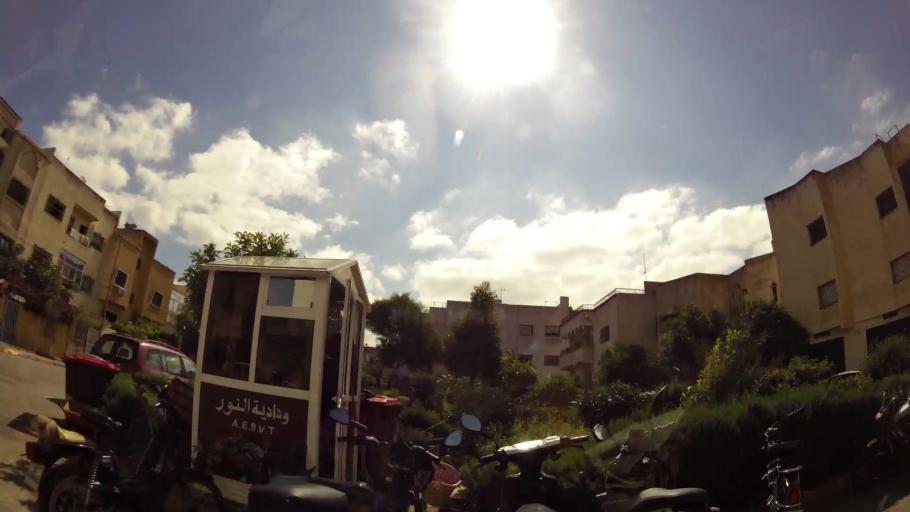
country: MA
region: Fes-Boulemane
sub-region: Fes
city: Fes
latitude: 34.0327
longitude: -5.0260
